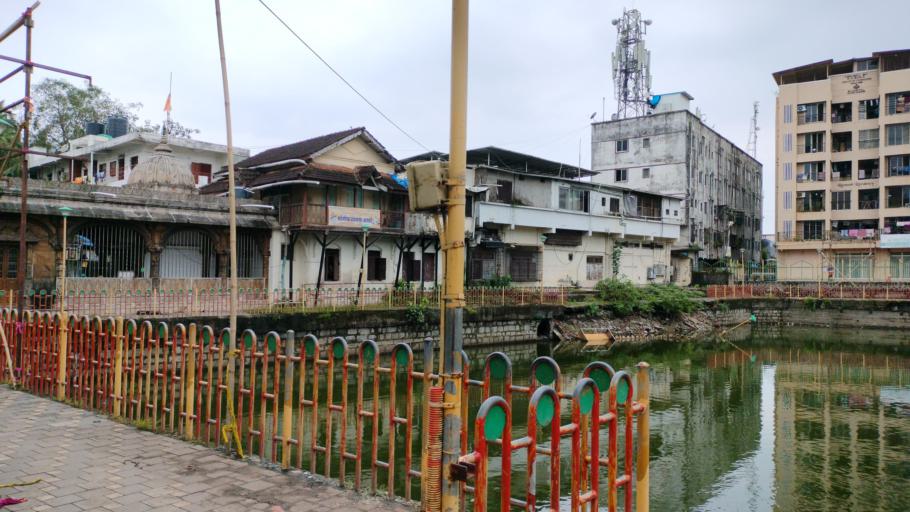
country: IN
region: Maharashtra
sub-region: Thane
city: Virar
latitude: 19.4633
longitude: 72.7762
